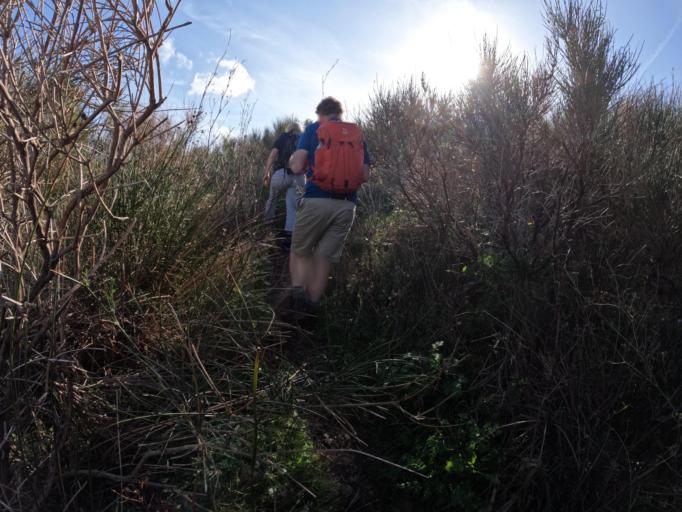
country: FR
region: Languedoc-Roussillon
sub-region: Departement des Pyrenees-Orientales
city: Banyuls de la Marenda
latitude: 42.4780
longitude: 3.1472
